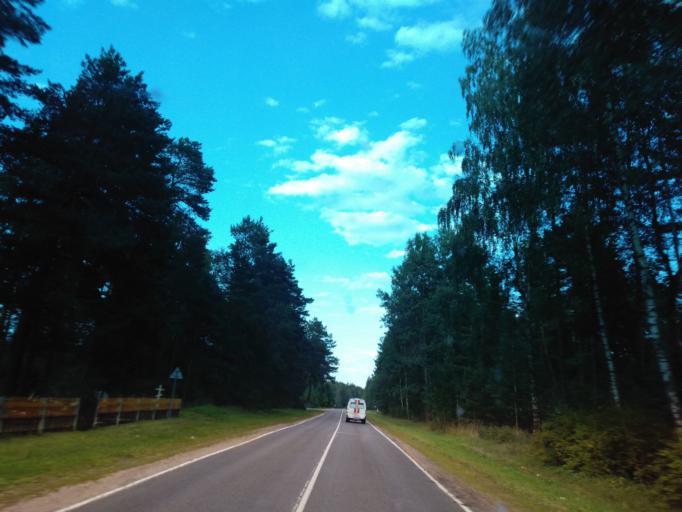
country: BY
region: Minsk
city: Uzda
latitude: 53.4188
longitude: 27.4169
